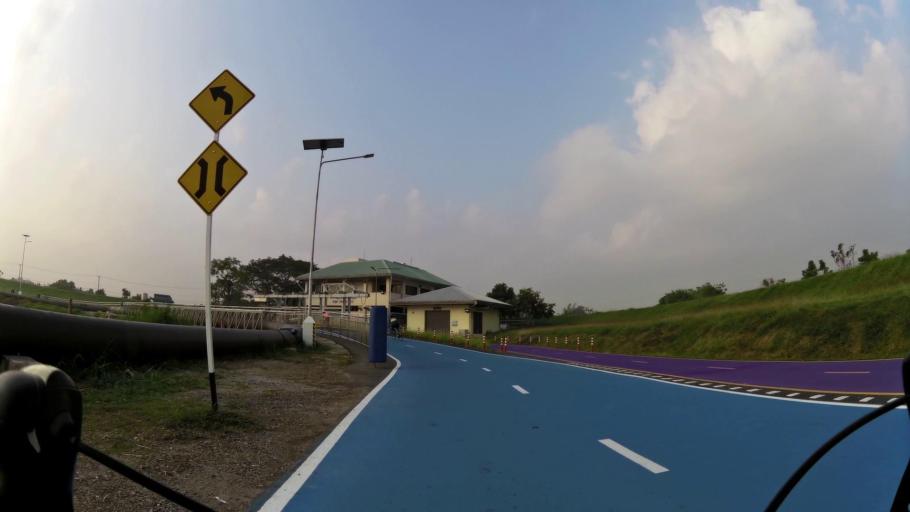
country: TH
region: Bangkok
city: Lat Krabang
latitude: 13.6951
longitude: 100.7737
